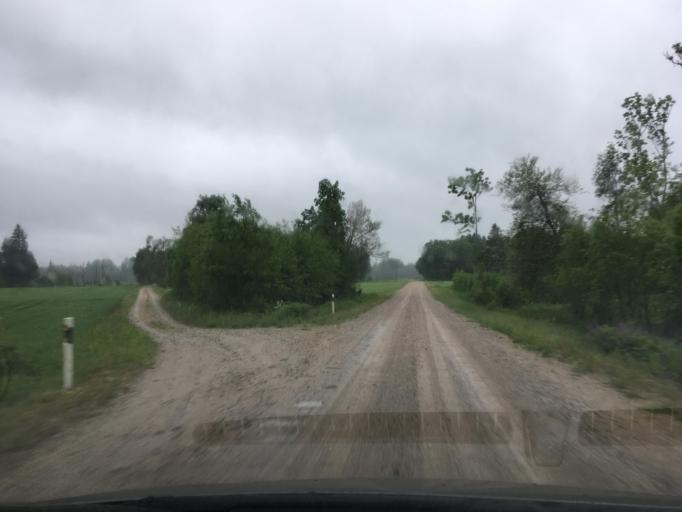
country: EE
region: Laeaene
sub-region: Lihula vald
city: Lihula
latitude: 58.6207
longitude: 23.8221
